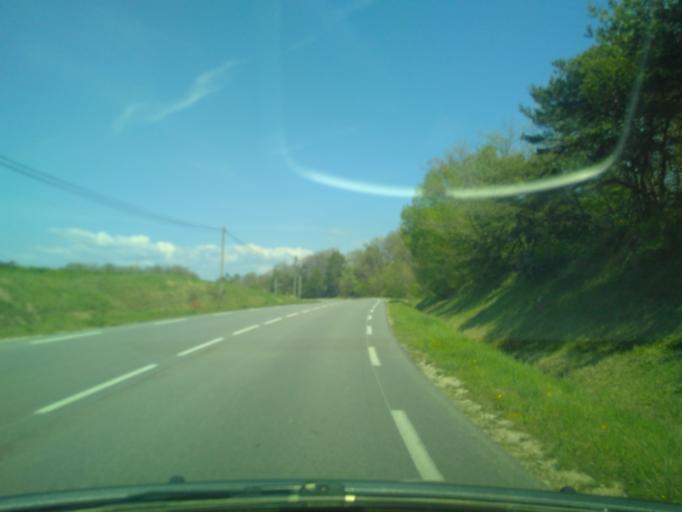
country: FR
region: Rhone-Alpes
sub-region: Departement de la Drome
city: Crest
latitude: 44.6656
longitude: 5.0021
